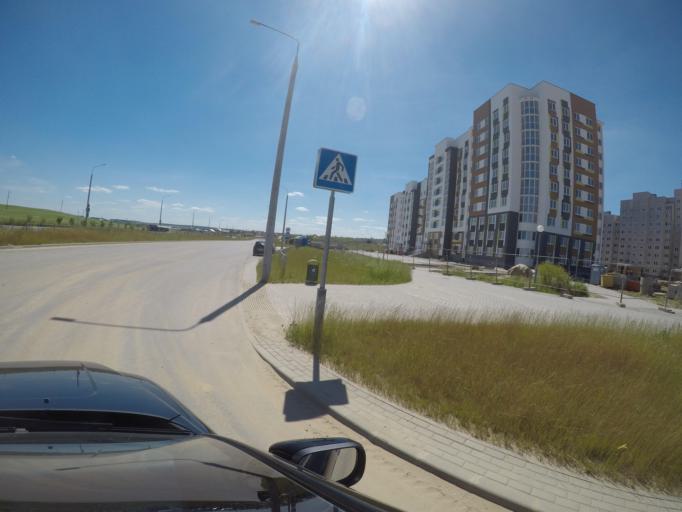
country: BY
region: Grodnenskaya
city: Hrodna
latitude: 53.7233
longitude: 23.8845
